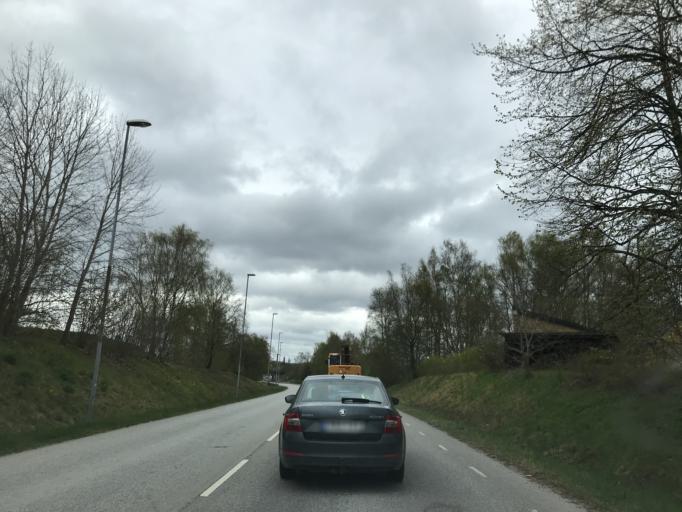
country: SE
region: Skane
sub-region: Hoors Kommun
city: Hoeoer
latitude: 55.9422
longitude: 13.5434
